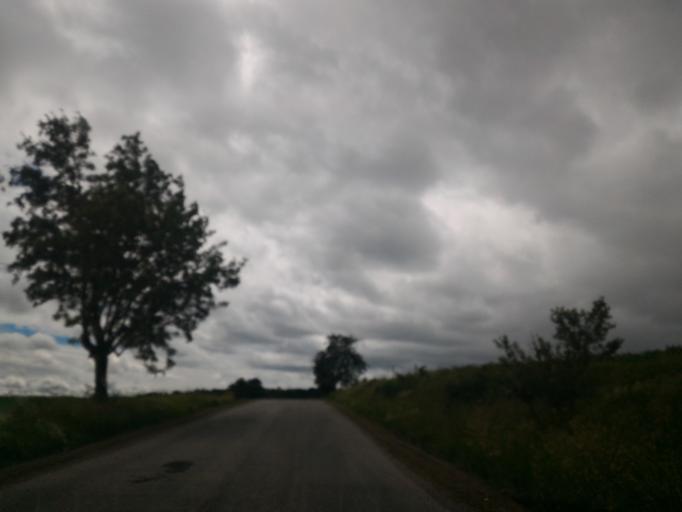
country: CZ
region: Vysocina
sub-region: Okres Jihlava
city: Telc
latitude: 49.2299
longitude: 15.4259
